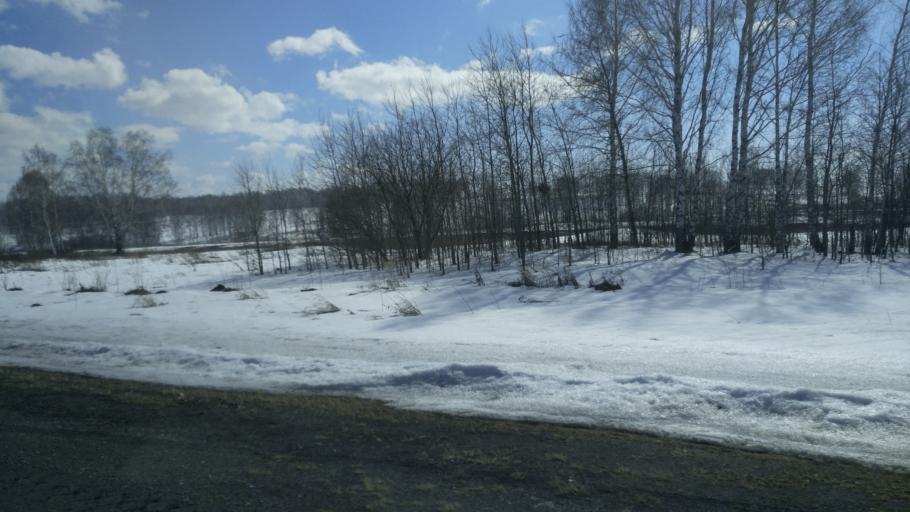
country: RU
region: Kemerovo
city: Yurga
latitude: 55.6848
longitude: 85.0558
